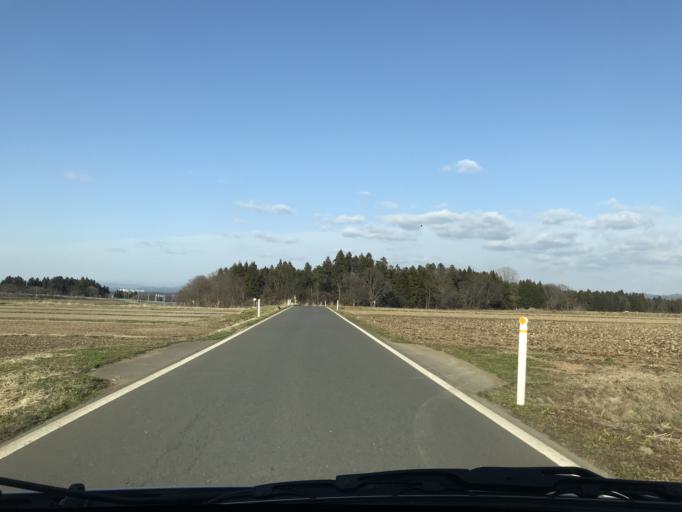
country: JP
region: Iwate
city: Kitakami
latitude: 39.2749
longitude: 141.0601
